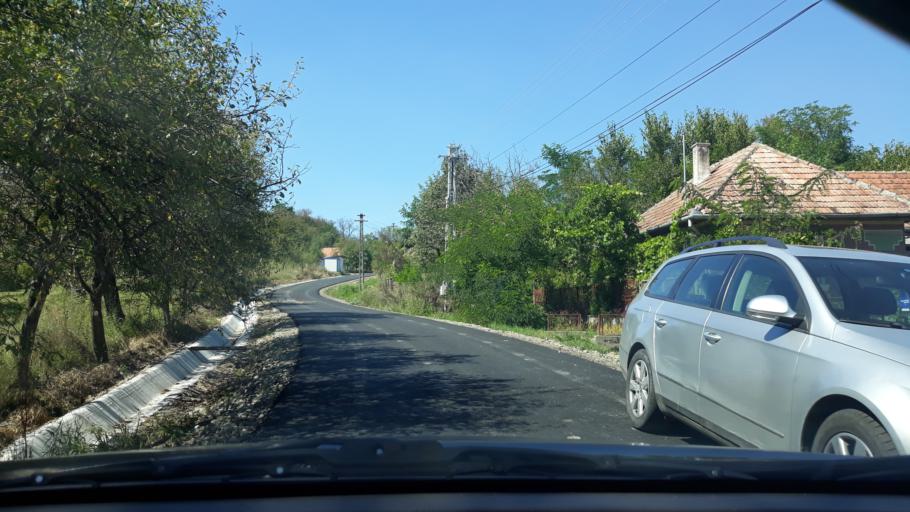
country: RO
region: Salaj
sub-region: Comuna Dobrin
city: Dobrin
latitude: 47.2913
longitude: 23.0919
